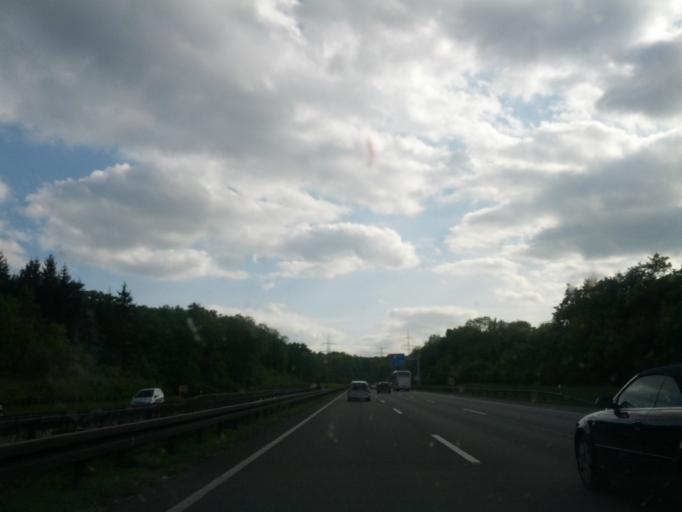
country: DE
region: Thuringia
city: Klettbach
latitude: 50.9344
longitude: 11.1516
